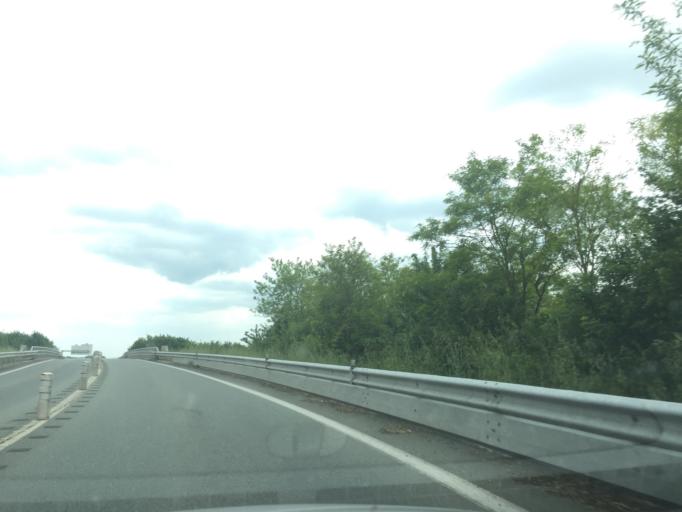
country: FR
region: Pays de la Loire
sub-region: Departement de la Vendee
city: Benet
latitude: 46.3917
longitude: -0.6568
